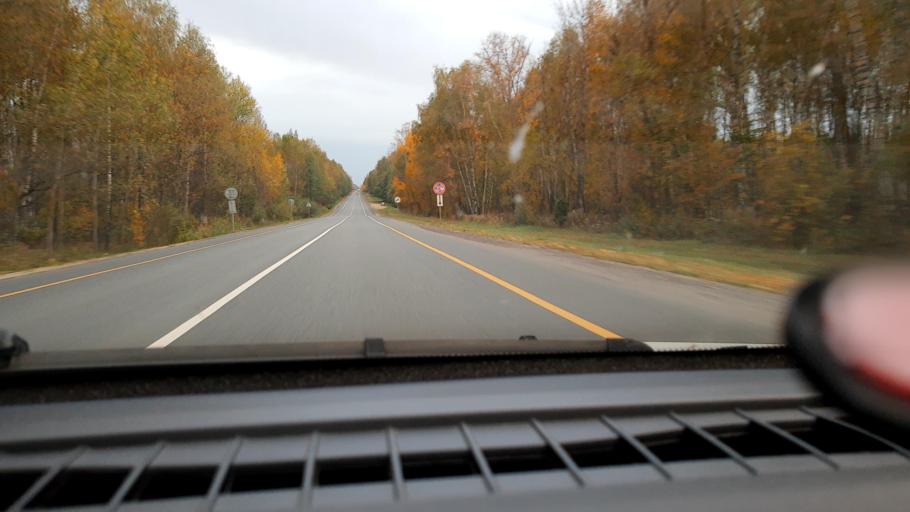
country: RU
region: Vladimir
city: Orgtrud
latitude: 56.2012
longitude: 40.7945
